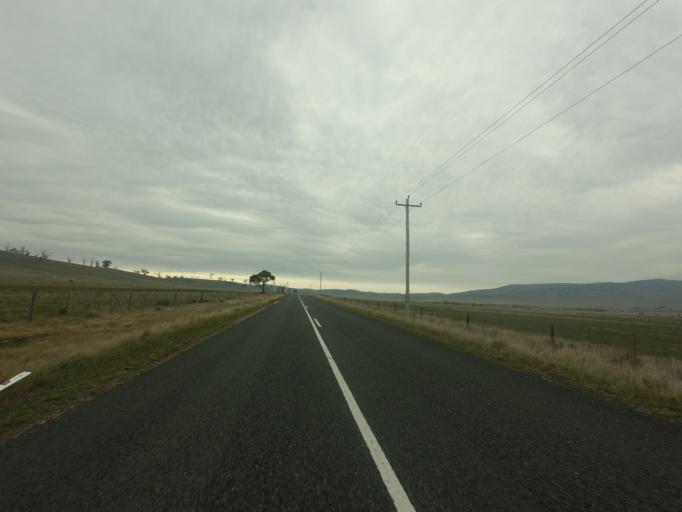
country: AU
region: Tasmania
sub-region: Derwent Valley
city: New Norfolk
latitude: -42.4403
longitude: 146.9779
